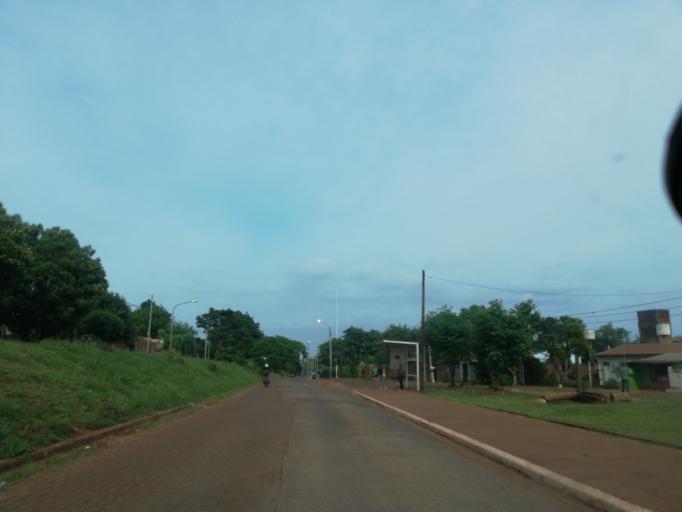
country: AR
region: Misiones
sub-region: Departamento de Capital
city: Posadas
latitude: -27.4362
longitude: -55.9115
